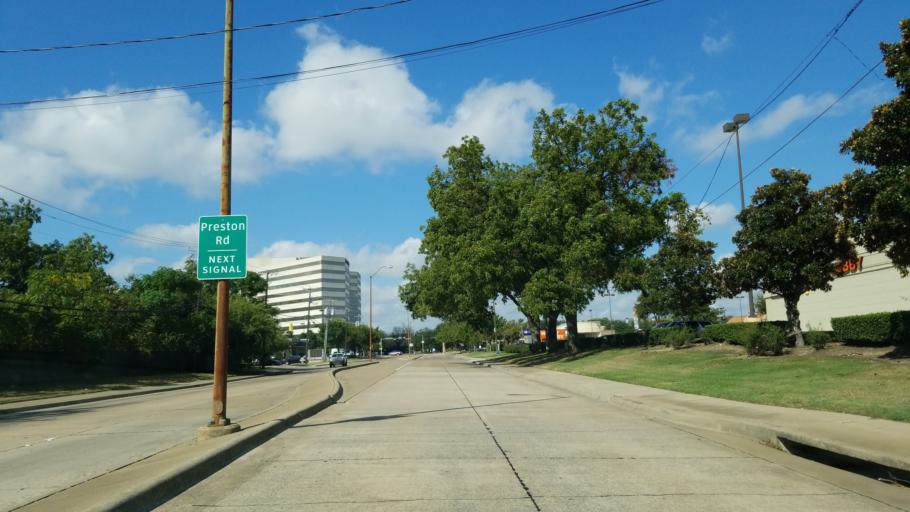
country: US
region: Texas
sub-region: Dallas County
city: Addison
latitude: 32.9499
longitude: -96.8006
